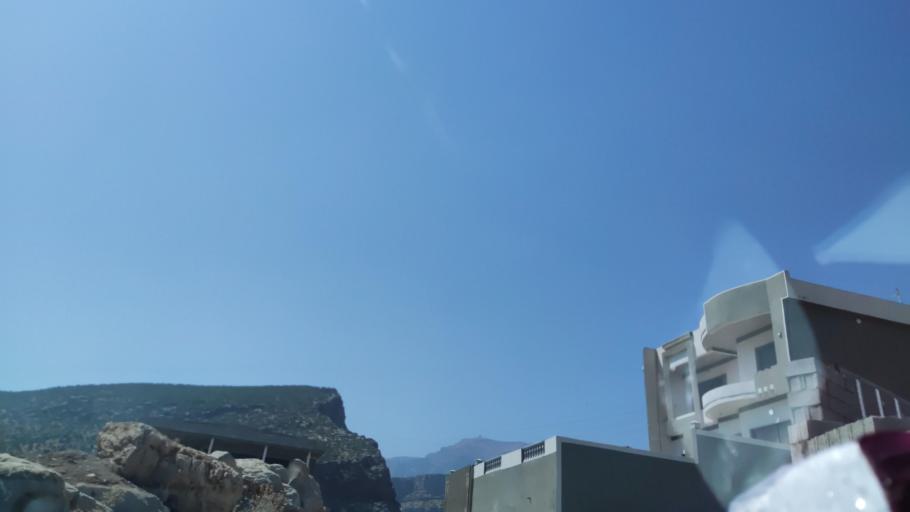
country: IQ
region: Arbil
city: Ruwandiz
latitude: 36.6492
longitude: 44.4969
